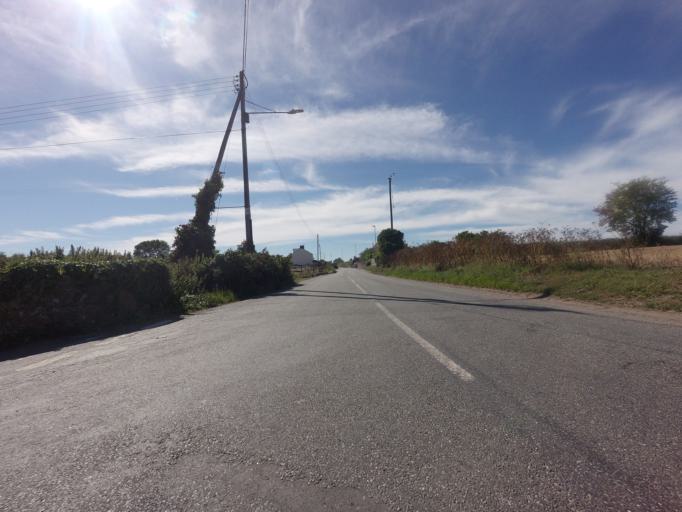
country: GB
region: England
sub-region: Kent
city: Birchington-on-Sea
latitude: 51.3367
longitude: 1.2938
